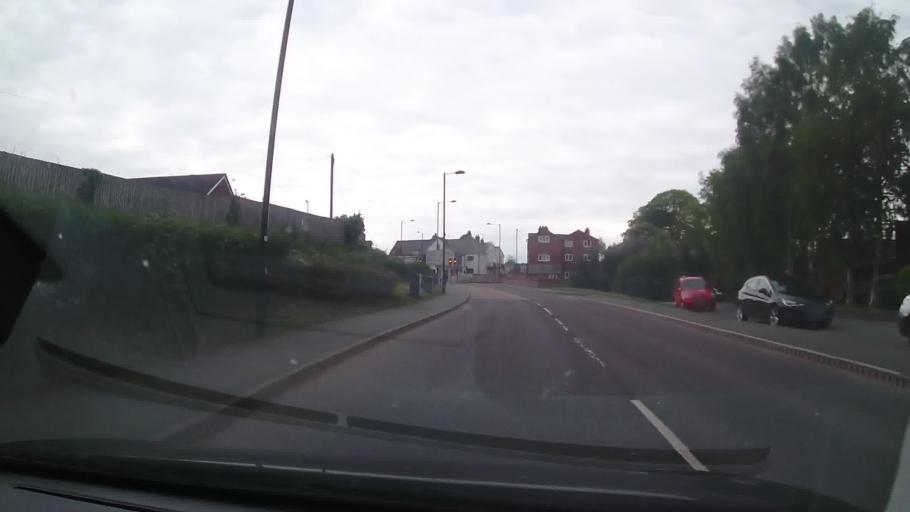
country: GB
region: England
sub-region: Shropshire
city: Ellesmere
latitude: 52.9049
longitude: -2.8976
